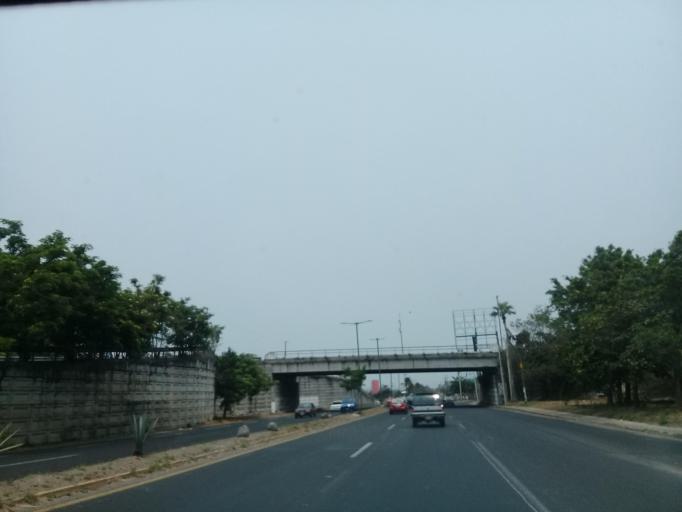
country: MX
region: Veracruz
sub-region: Veracruz
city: Hacienda Sotavento
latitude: 19.1502
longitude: -96.1750
